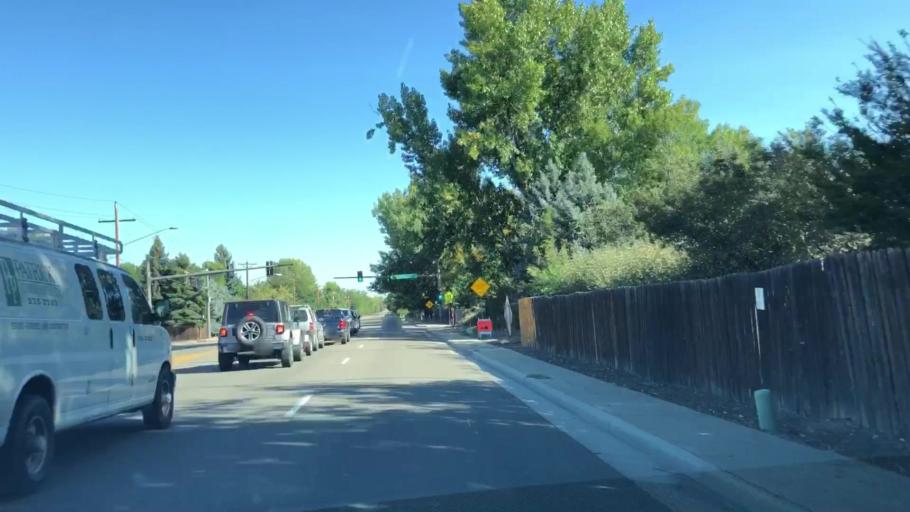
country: US
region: Colorado
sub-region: Larimer County
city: Loveland
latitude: 40.4154
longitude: -105.0586
